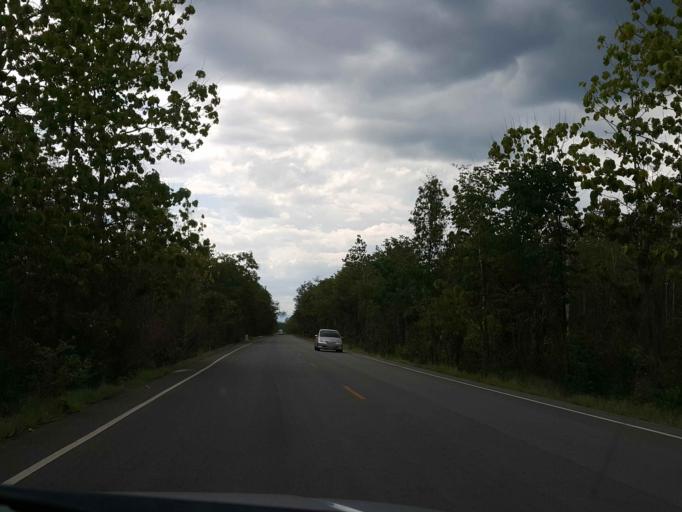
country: TH
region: Sukhothai
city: Thung Saliam
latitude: 17.3679
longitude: 99.4071
